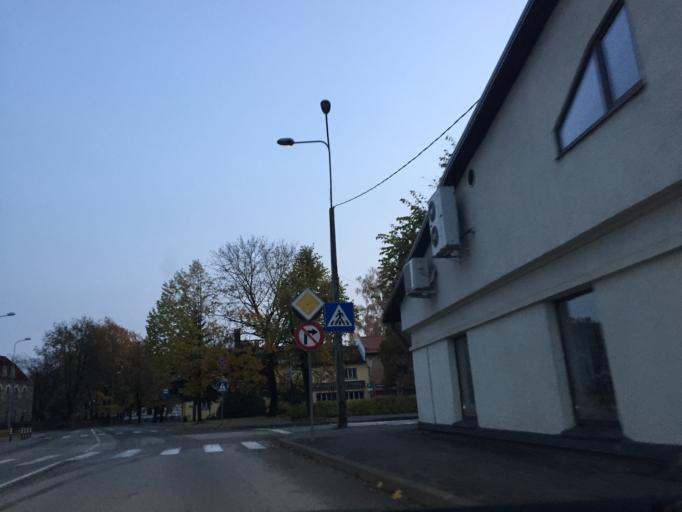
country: LV
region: Cesu Rajons
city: Cesis
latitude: 57.3149
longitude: 25.2789
